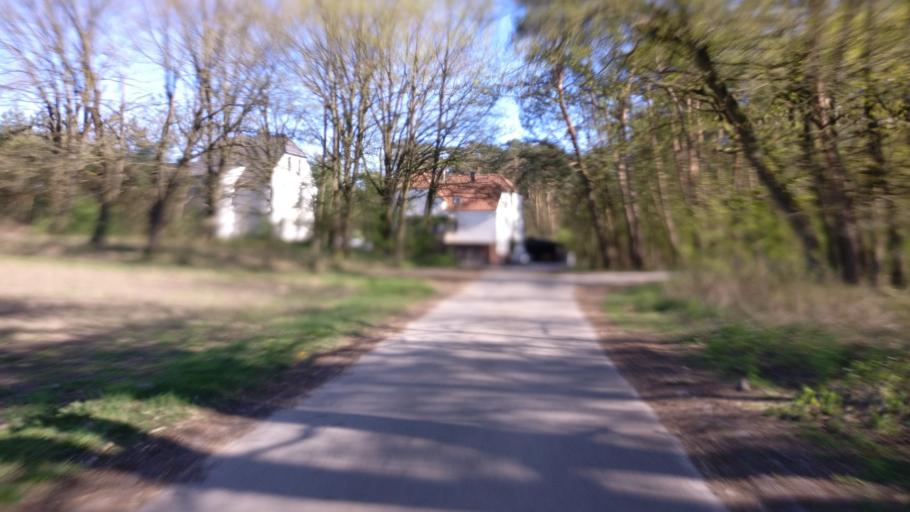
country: DE
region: North Rhine-Westphalia
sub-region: Regierungsbezirk Detmold
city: Lage
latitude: 52.0128
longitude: 8.7656
